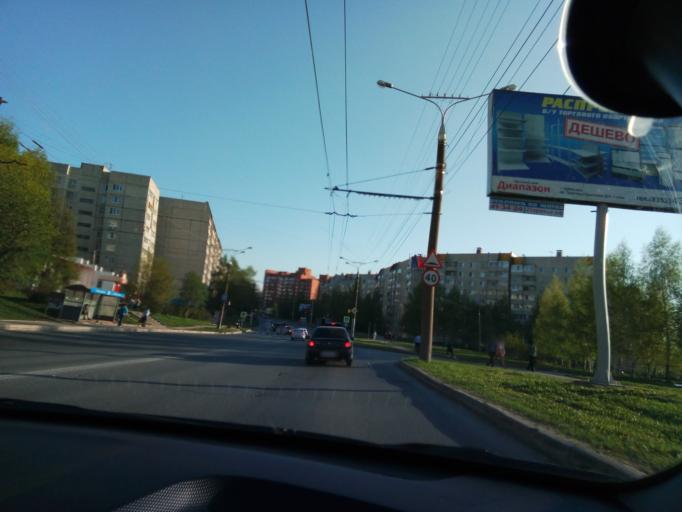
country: RU
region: Chuvashia
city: Novyye Lapsary
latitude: 56.1409
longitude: 47.1646
